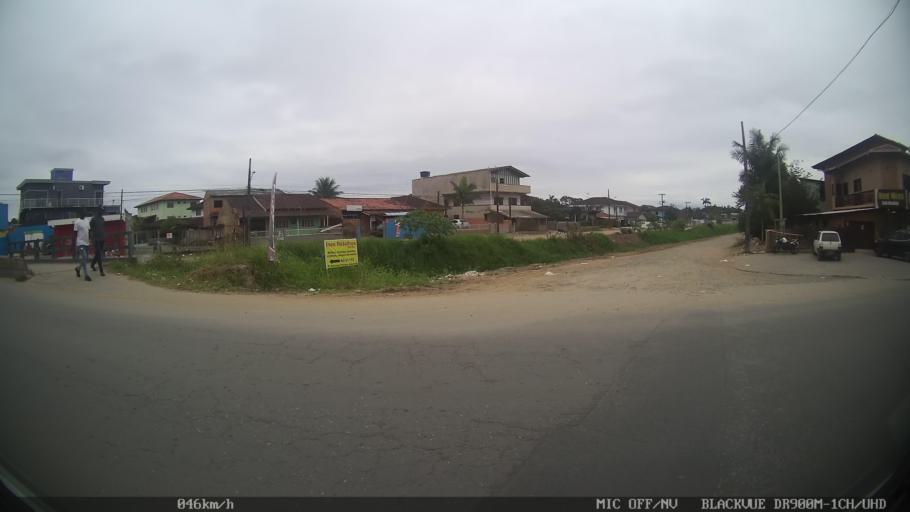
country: BR
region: Santa Catarina
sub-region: Joinville
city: Joinville
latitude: -26.3359
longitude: -48.8169
